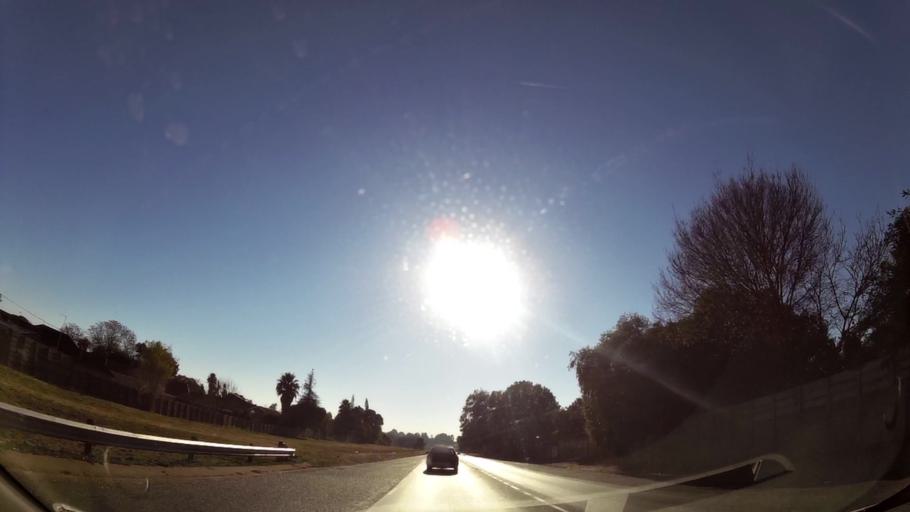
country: ZA
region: Gauteng
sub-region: Ekurhuleni Metropolitan Municipality
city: Tembisa
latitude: -26.0491
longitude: 28.2400
